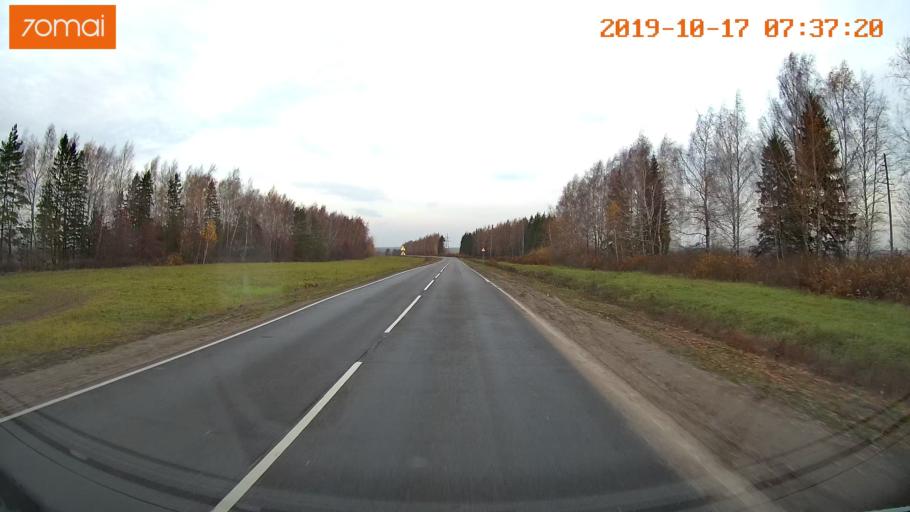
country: RU
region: Vladimir
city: Yur'yev-Pol'skiy
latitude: 56.4487
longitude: 39.9015
